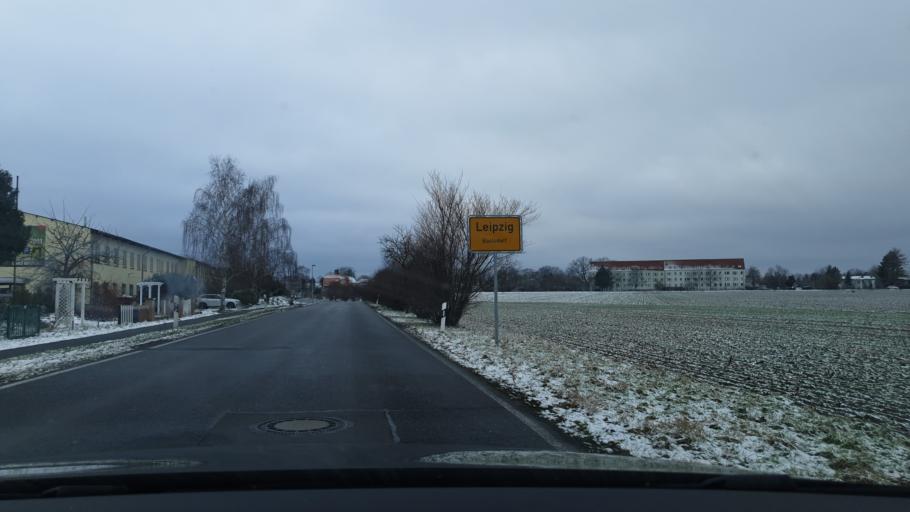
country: DE
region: Saxony
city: Borsdorf
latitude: 51.3241
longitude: 12.4927
